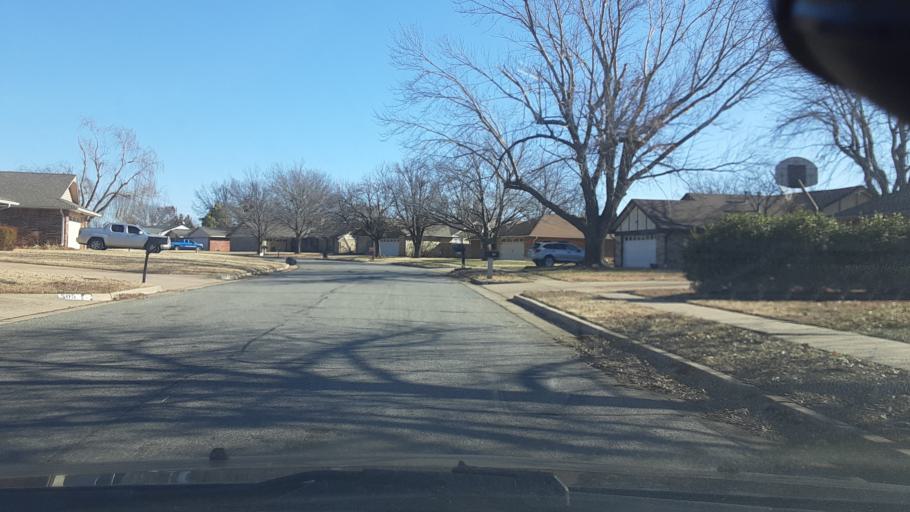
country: US
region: Oklahoma
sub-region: Kay County
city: Ponca City
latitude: 36.7294
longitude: -97.0883
